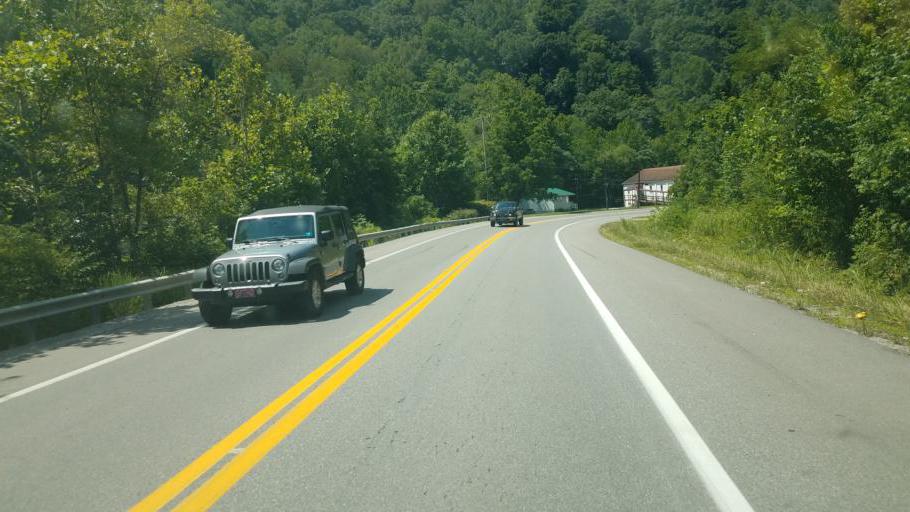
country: US
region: West Virginia
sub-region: Kanawha County
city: Chesapeake
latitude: 38.1626
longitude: -81.4503
